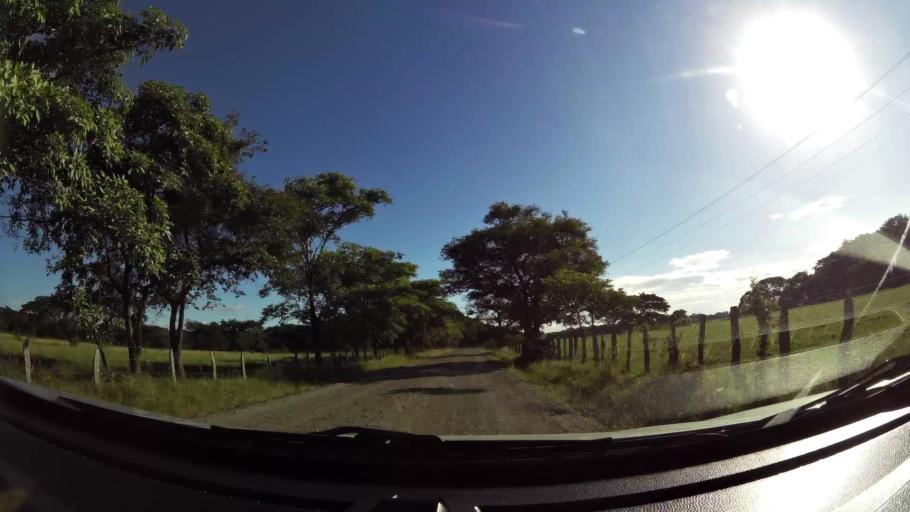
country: CR
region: Guanacaste
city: Sardinal
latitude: 10.4841
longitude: -85.5896
